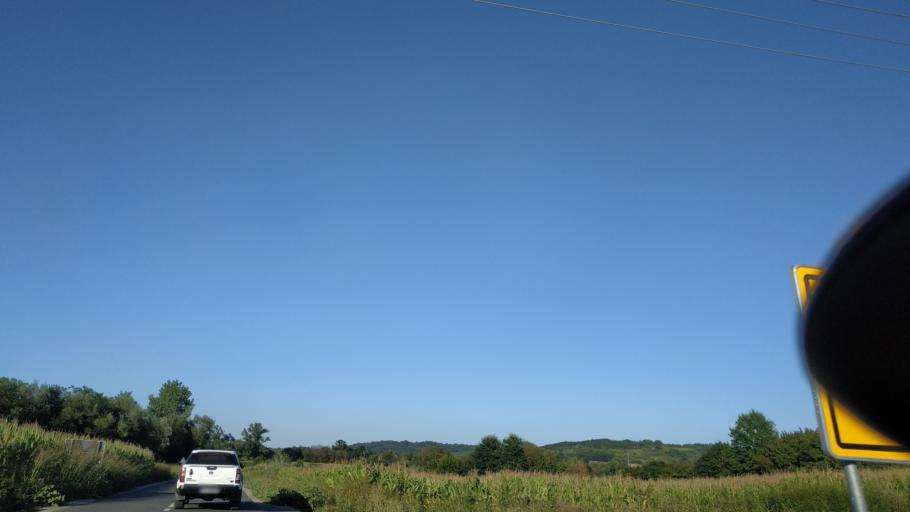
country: RS
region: Central Serbia
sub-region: Rasinski Okrug
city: Krusevac
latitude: 43.5268
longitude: 21.3378
